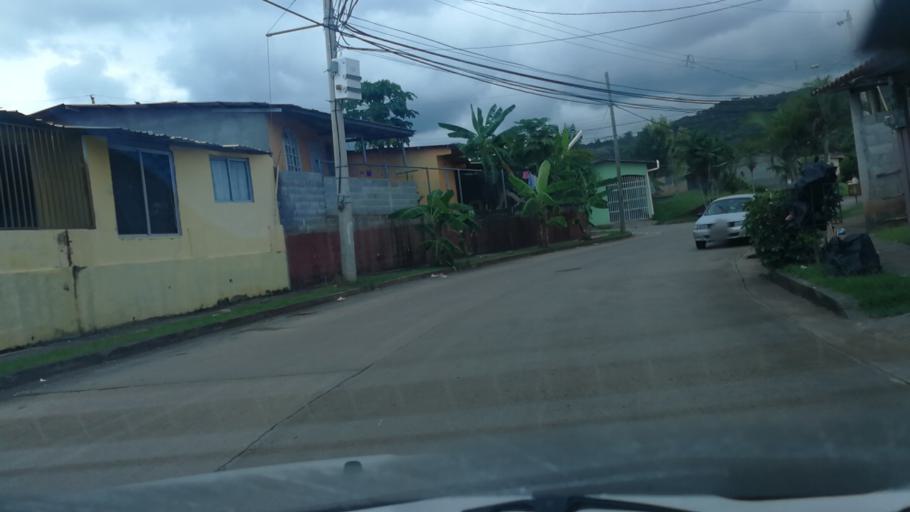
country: PA
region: Panama
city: Tocumen
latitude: 9.1087
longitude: -79.3775
